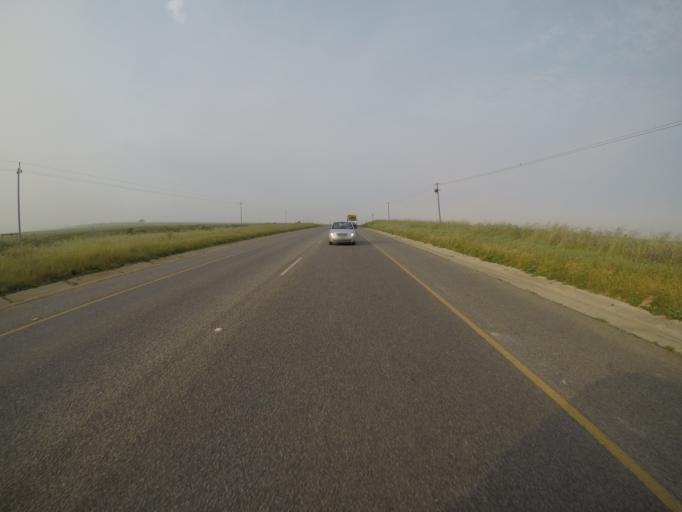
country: ZA
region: Western Cape
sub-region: West Coast District Municipality
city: Malmesbury
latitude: -33.6500
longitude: 18.7108
